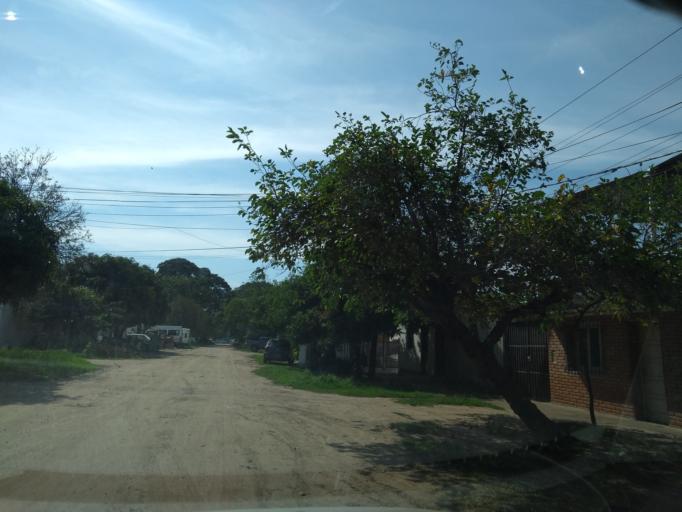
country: AR
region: Chaco
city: Barranqueras
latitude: -27.4788
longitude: -58.9619
